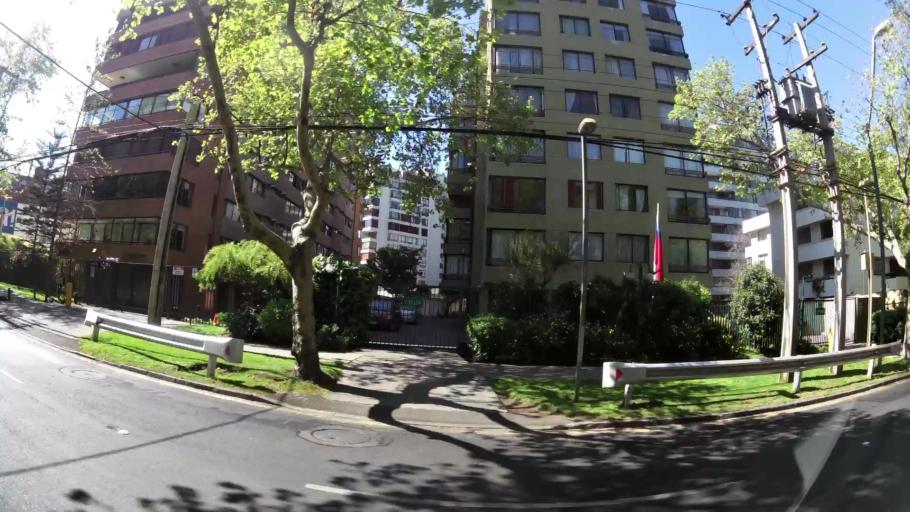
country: CL
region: Santiago Metropolitan
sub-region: Provincia de Santiago
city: Villa Presidente Frei, Nunoa, Santiago, Chile
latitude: -33.4205
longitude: -70.5758
